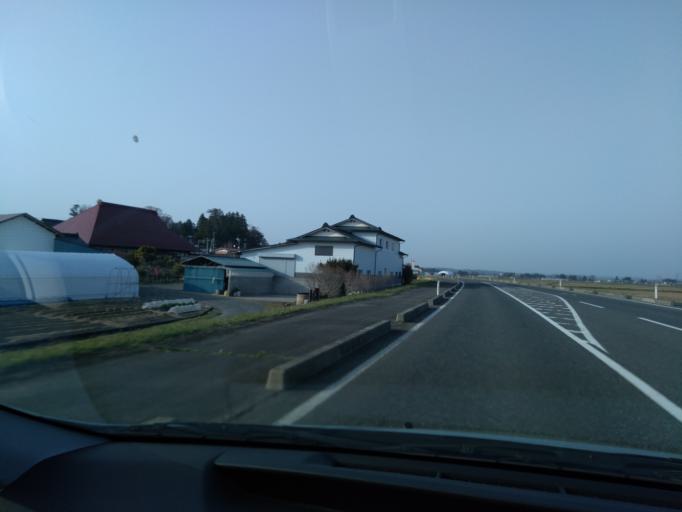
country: JP
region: Iwate
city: Ichinoseki
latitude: 38.7401
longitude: 141.1303
